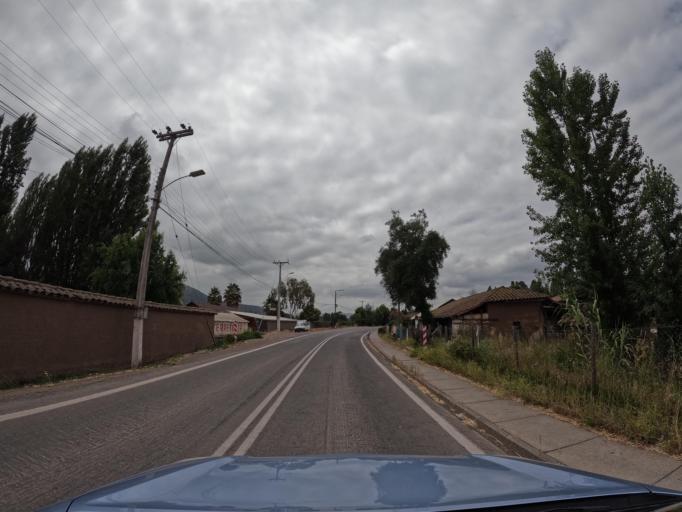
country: CL
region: Maule
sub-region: Provincia de Curico
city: Teno
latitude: -34.7593
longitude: -71.2031
